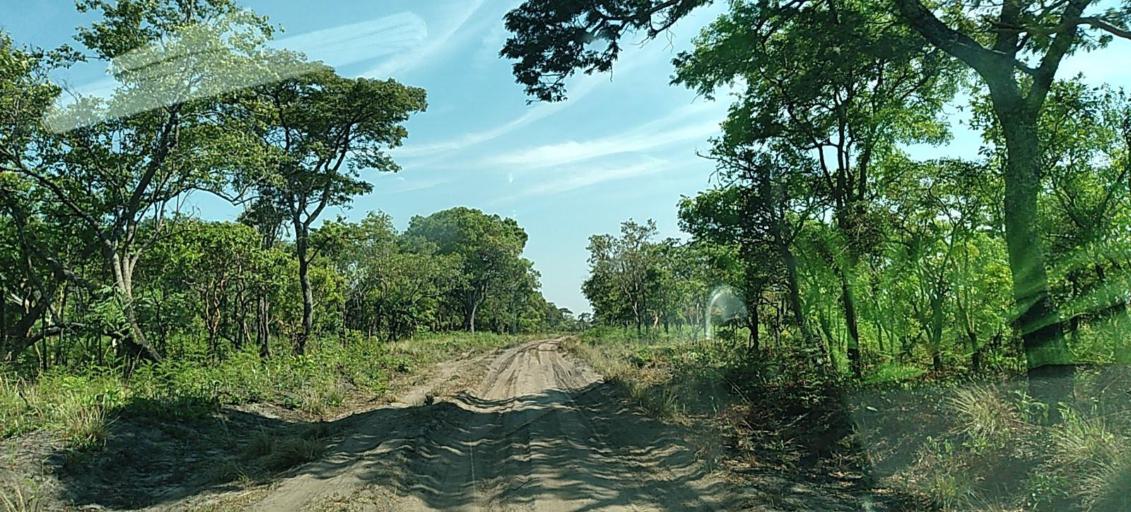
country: ZM
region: North-Western
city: Mwinilunga
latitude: -11.7935
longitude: 25.1673
